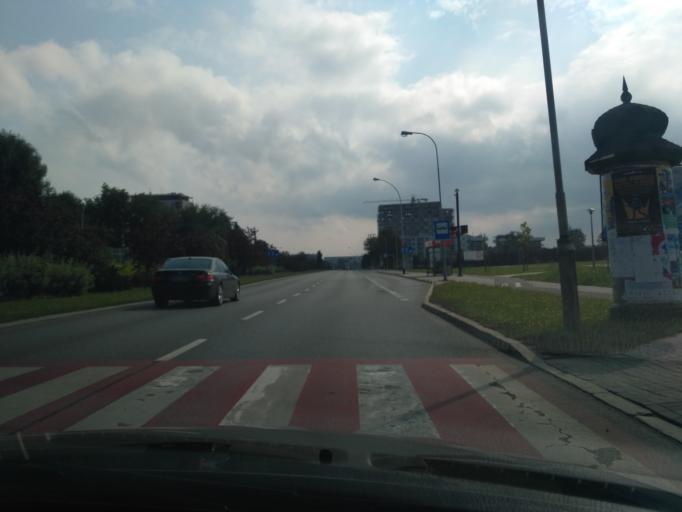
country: PL
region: Subcarpathian Voivodeship
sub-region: Rzeszow
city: Rzeszow
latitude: 50.0202
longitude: 21.9880
